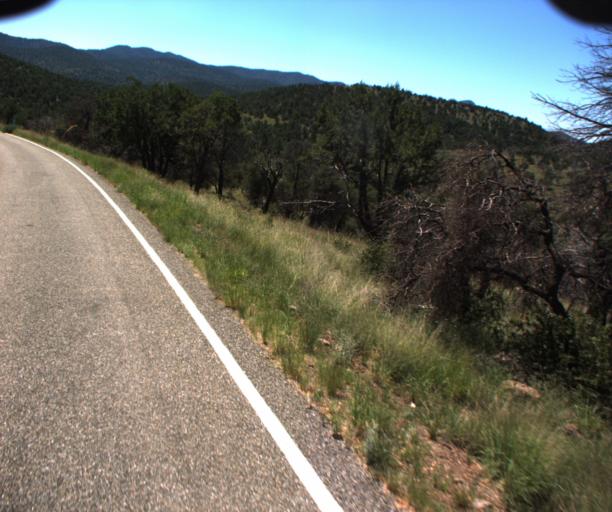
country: US
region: Arizona
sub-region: Greenlee County
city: Morenci
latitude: 33.2873
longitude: -109.3559
